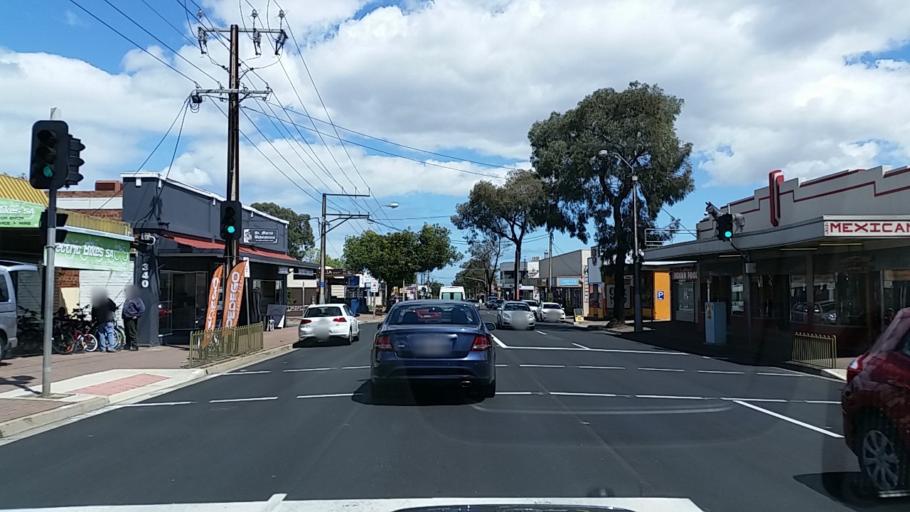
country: AU
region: South Australia
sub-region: Norwood Payneham St Peters
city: Trinity Gardens
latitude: -34.9142
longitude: 138.6532
